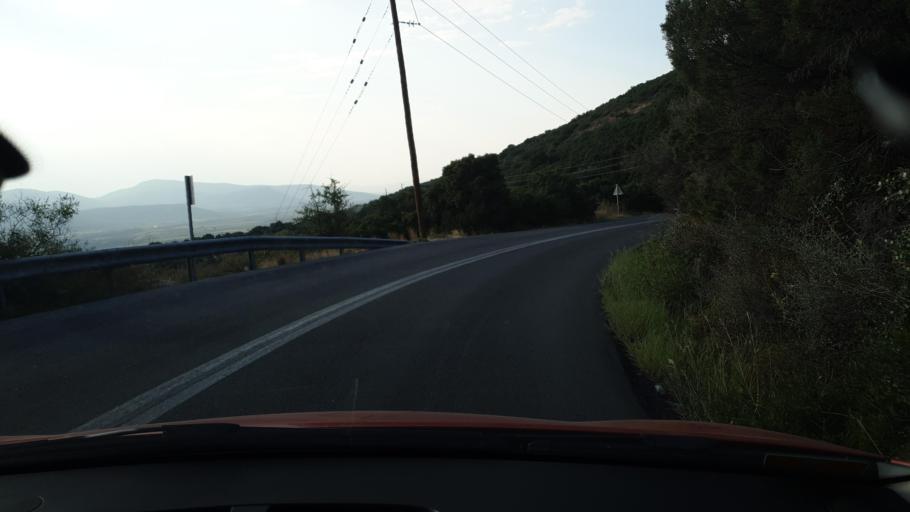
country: GR
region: Thessaly
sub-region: Nomos Magnisias
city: Pteleos
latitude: 39.0639
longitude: 22.9275
